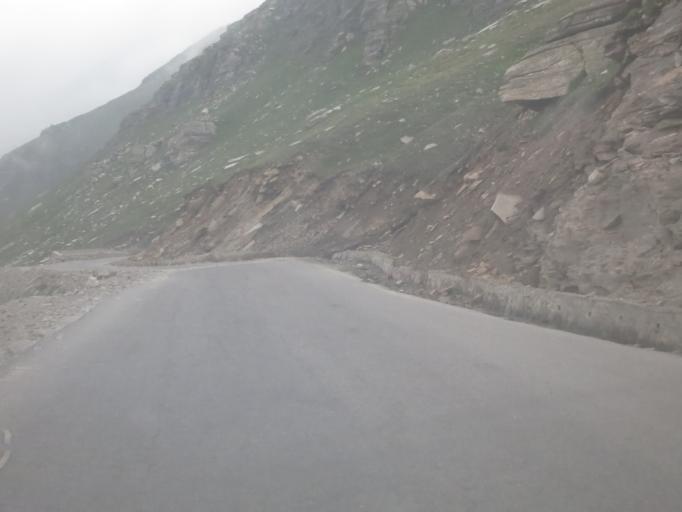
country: IN
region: Himachal Pradesh
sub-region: Kulu
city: Manali
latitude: 32.3655
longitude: 77.2413
